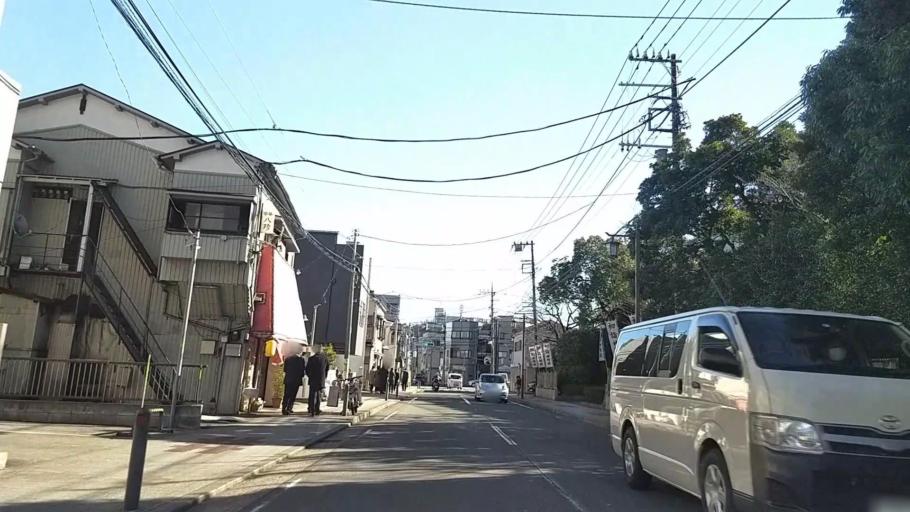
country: JP
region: Kanagawa
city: Yokohama
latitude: 35.4525
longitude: 139.5992
